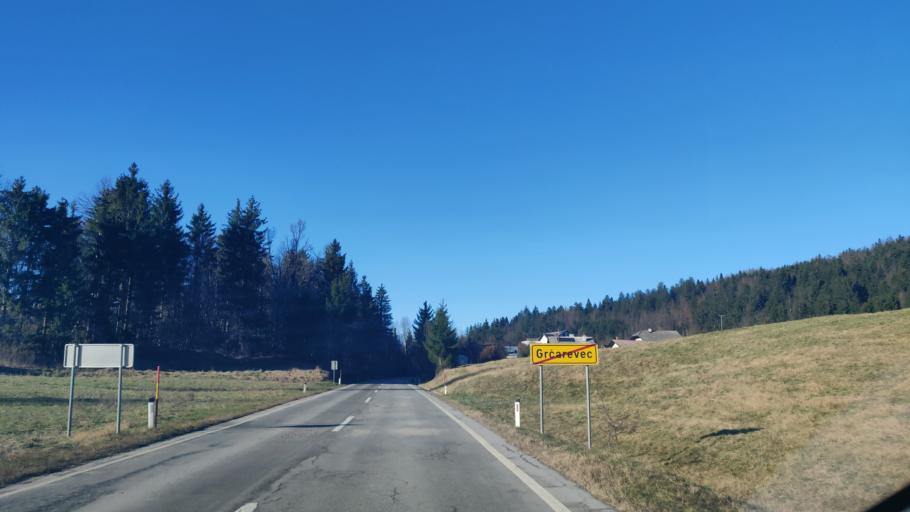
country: SI
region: Logatec
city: Logatec
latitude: 45.8758
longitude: 14.2113
